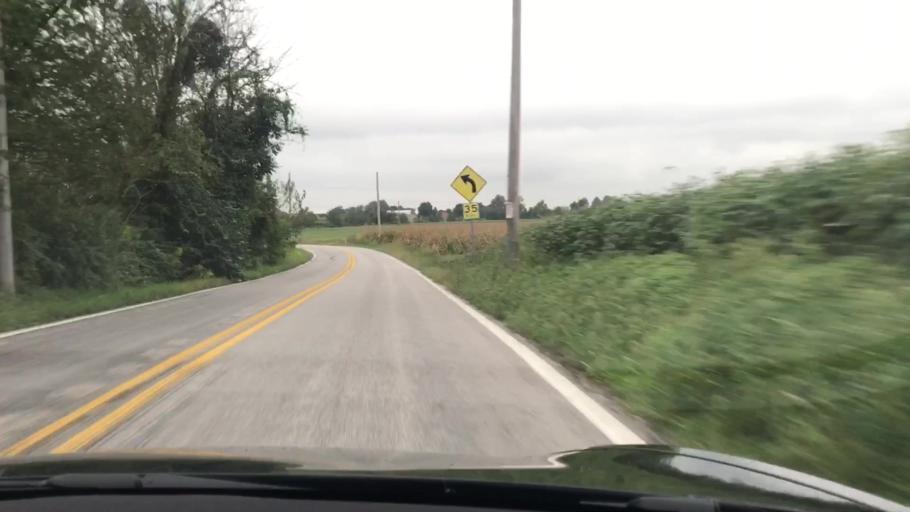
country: US
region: Pennsylvania
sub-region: York County
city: Weigelstown
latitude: 39.9528
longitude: -76.8615
